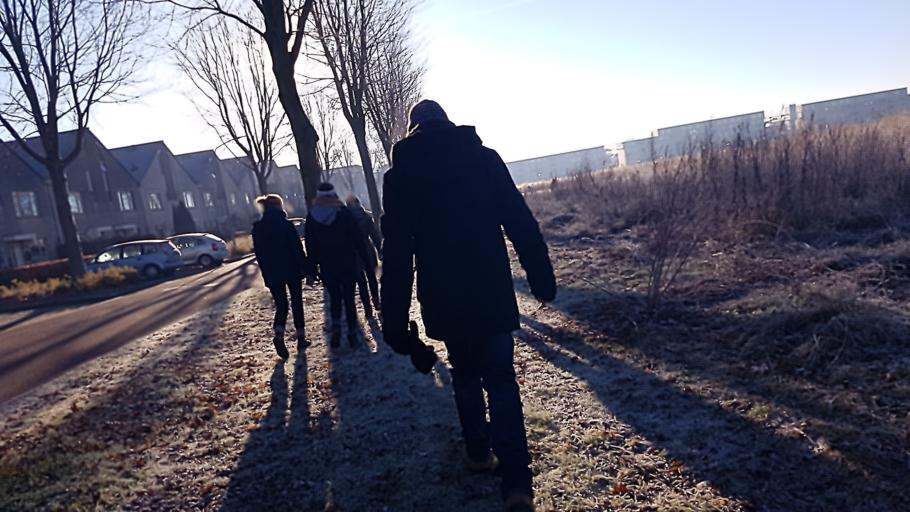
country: NL
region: Flevoland
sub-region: Gemeente Almere
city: Almere Stad
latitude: 52.3757
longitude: 5.2289
